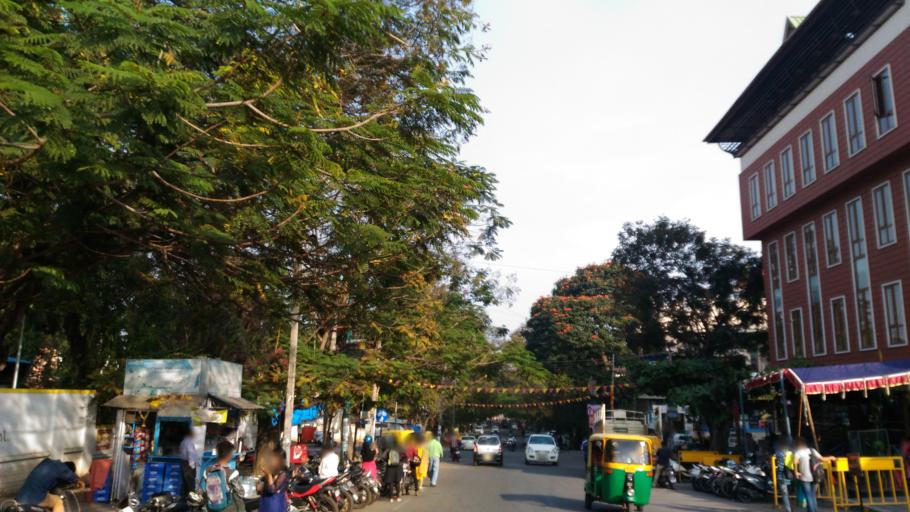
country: IN
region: Karnataka
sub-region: Bangalore Urban
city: Bangalore
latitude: 12.9232
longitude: 77.5929
